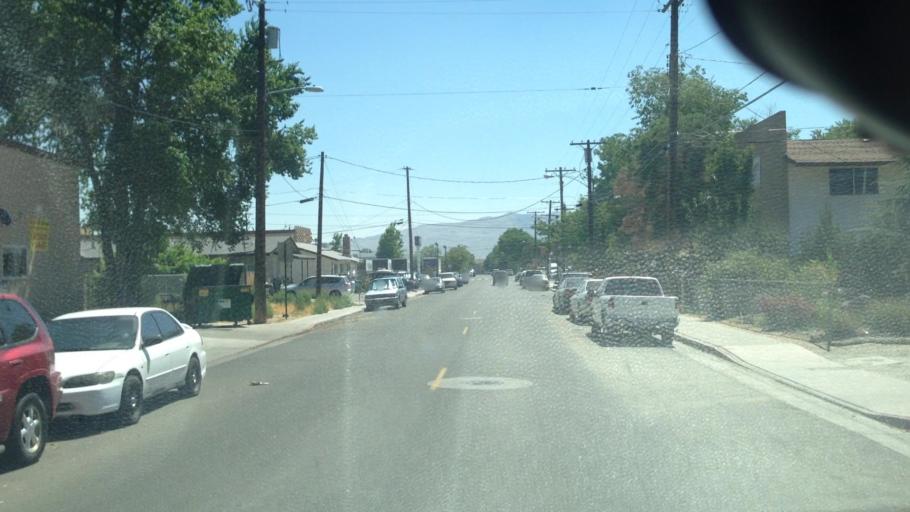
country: US
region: Nevada
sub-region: Washoe County
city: Reno
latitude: 39.4996
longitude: -119.7914
